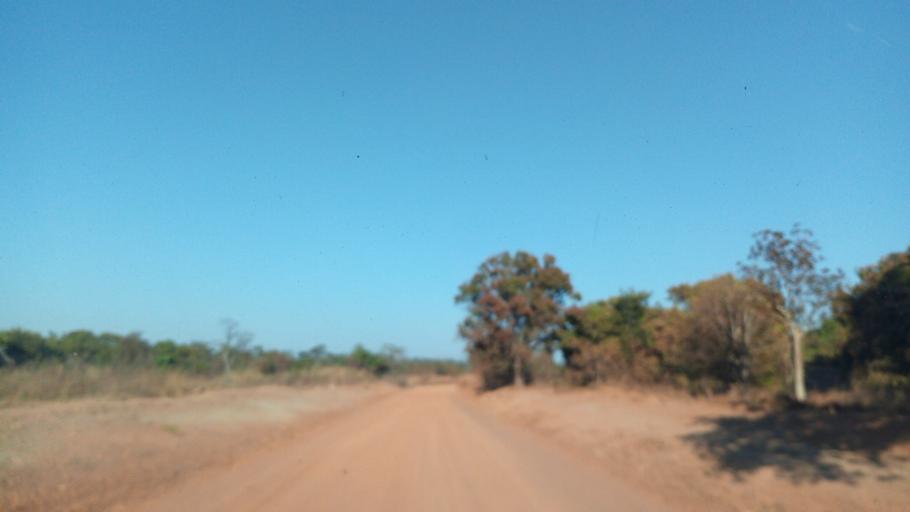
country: ZM
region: Luapula
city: Mwense
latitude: -10.4824
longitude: 28.5057
